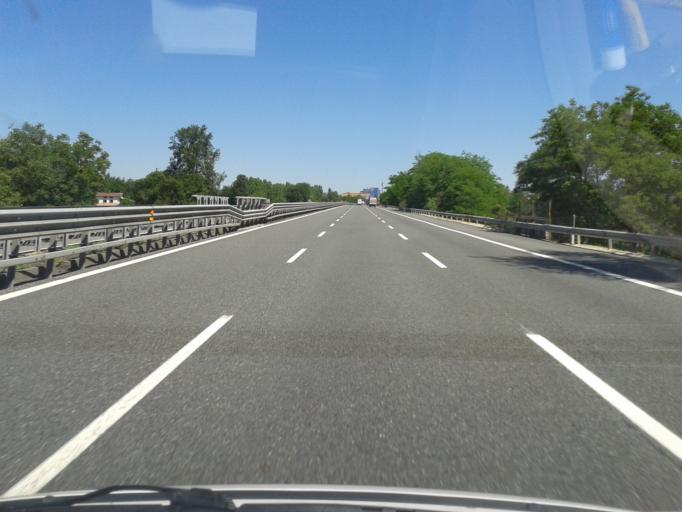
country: IT
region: Piedmont
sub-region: Provincia di Alessandria
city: Silvano d'Orba
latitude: 44.7091
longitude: 8.6674
